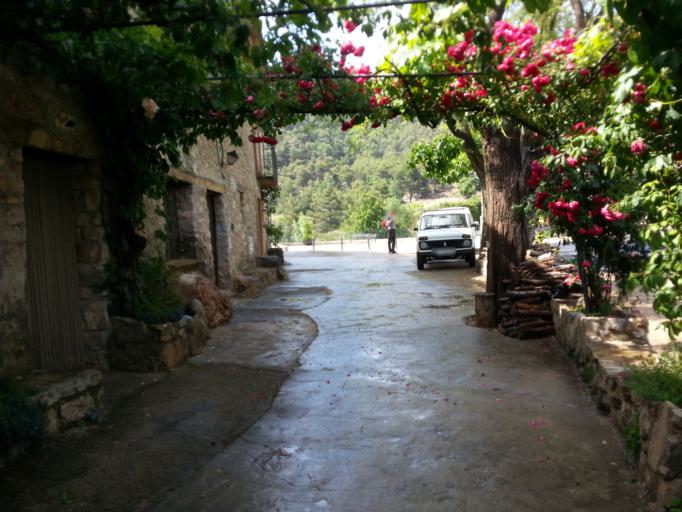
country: ES
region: Catalonia
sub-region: Provincia de Tarragona
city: Mont-ral
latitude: 41.3115
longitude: 1.0871
